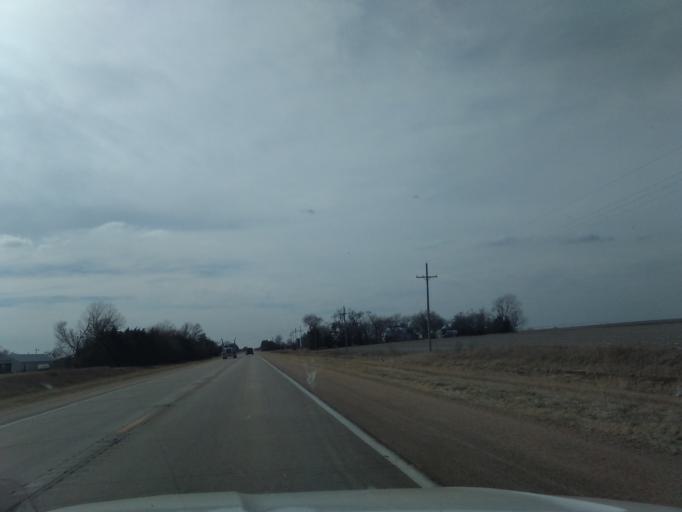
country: US
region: Nebraska
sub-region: Jefferson County
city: Fairbury
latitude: 40.1901
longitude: -97.0436
